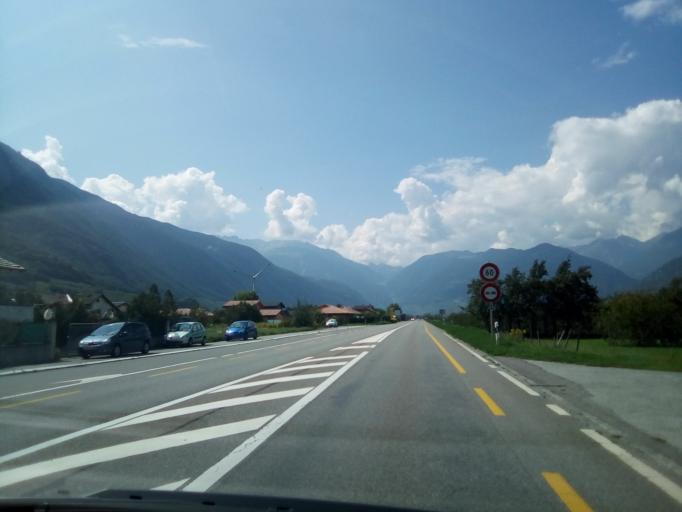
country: CH
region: Valais
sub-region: Martigny District
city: Saxon
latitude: 46.1402
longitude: 7.1554
